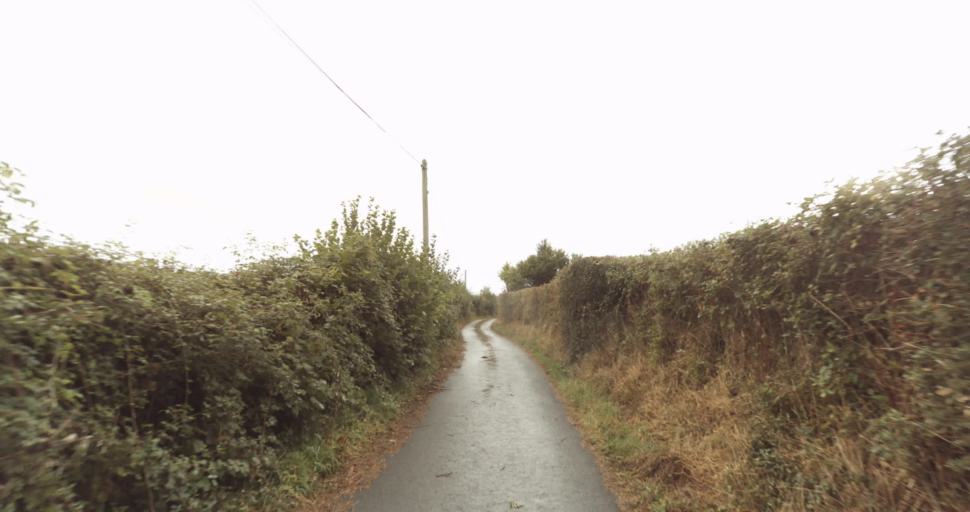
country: FR
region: Lower Normandy
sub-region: Departement de l'Orne
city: Vimoutiers
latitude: 48.8989
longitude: 0.1982
